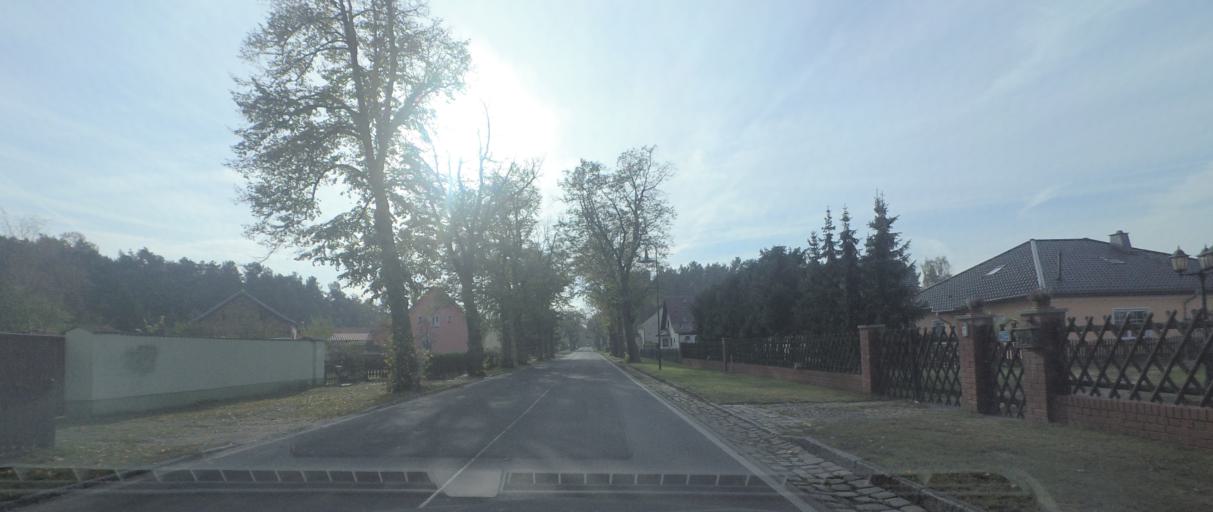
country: DE
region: Brandenburg
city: Am Mellensee
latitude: 52.2137
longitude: 13.4030
